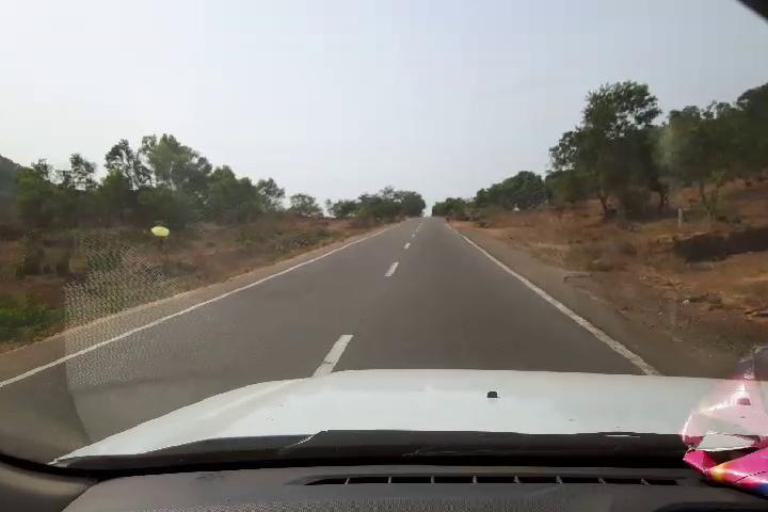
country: SL
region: Western Area
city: Waterloo
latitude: 8.2090
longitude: -13.1332
